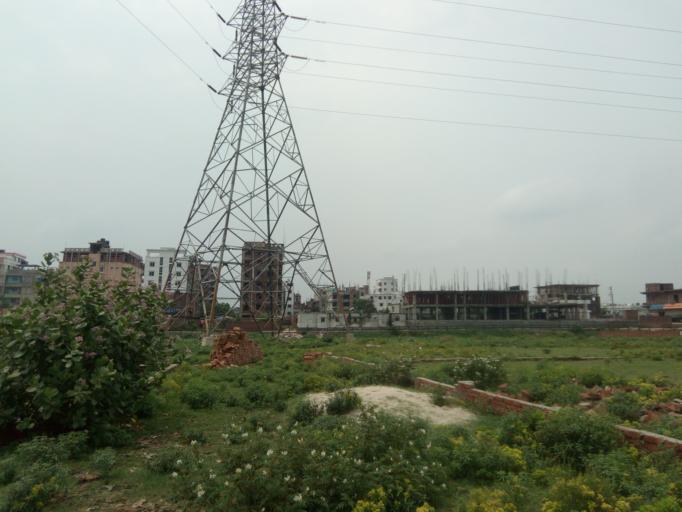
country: BD
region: Dhaka
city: Azimpur
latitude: 23.7426
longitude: 90.3519
